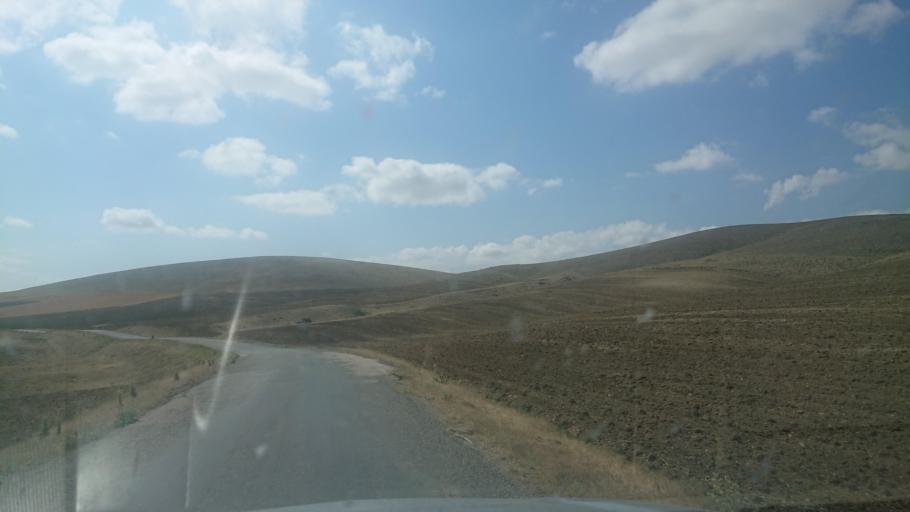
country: TR
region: Aksaray
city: Sariyahsi
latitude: 39.0040
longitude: 33.9613
